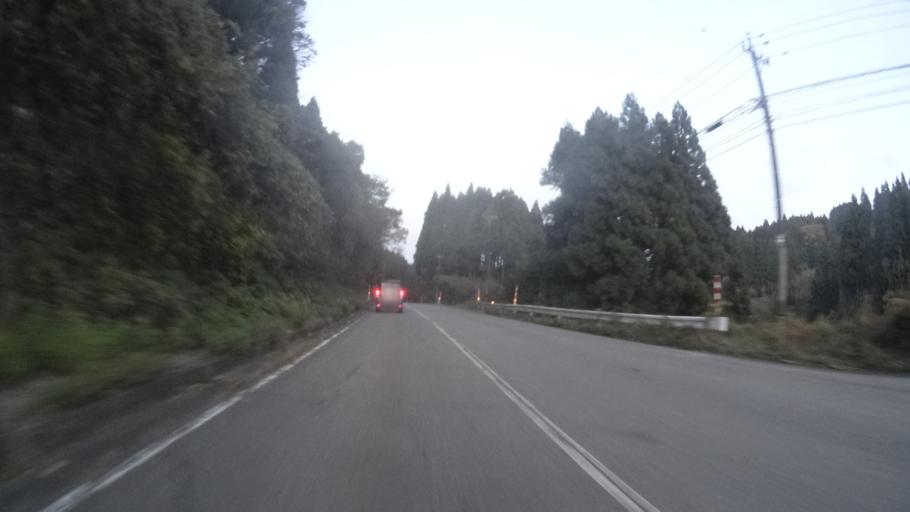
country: JP
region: Ishikawa
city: Nanao
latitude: 37.3428
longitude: 136.8442
